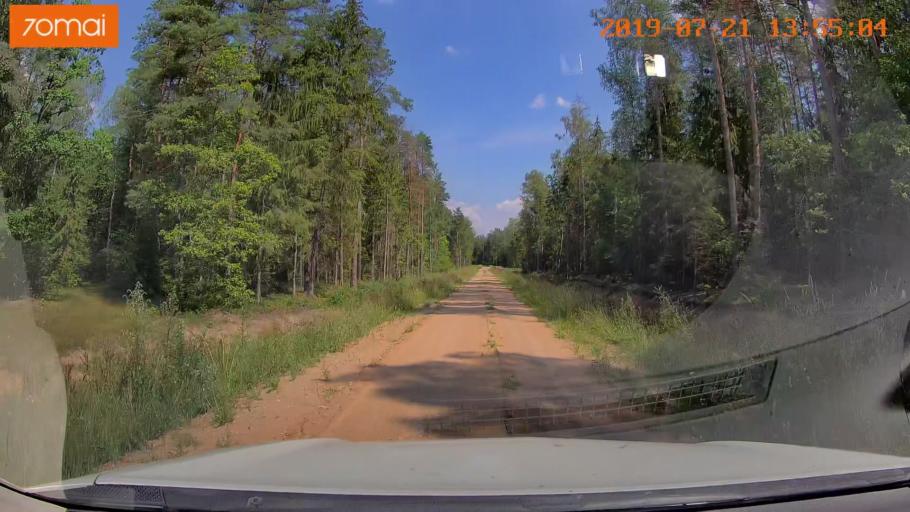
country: BY
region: Grodnenskaya
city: Lyubcha
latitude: 53.7792
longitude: 26.0817
